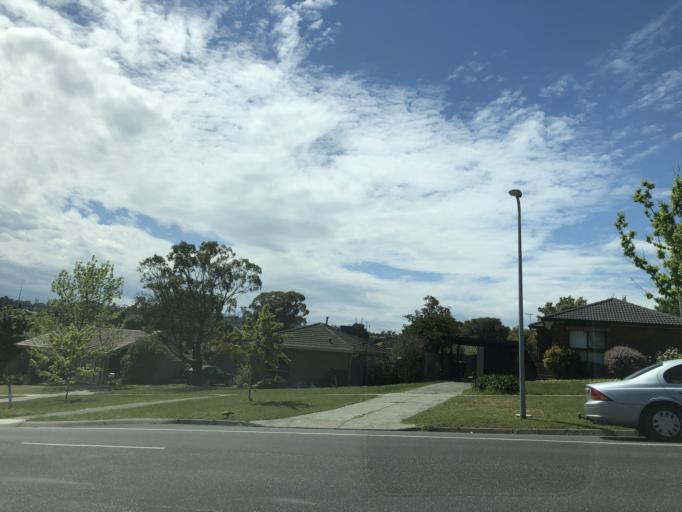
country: AU
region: Victoria
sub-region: Casey
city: Endeavour Hills
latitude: -37.9703
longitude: 145.2609
